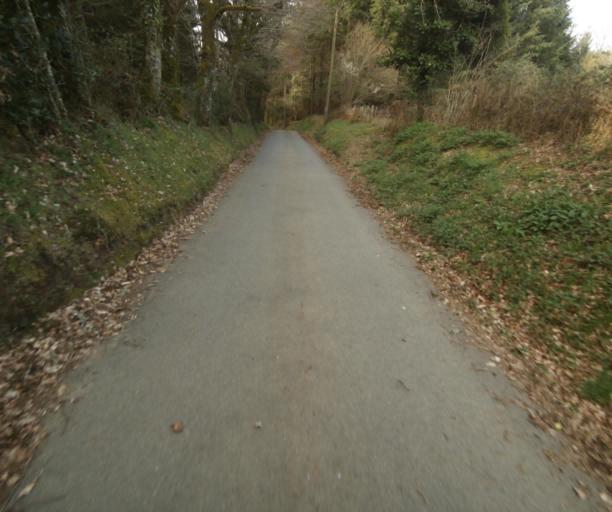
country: FR
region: Limousin
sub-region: Departement de la Correze
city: Correze
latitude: 45.4202
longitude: 1.8008
